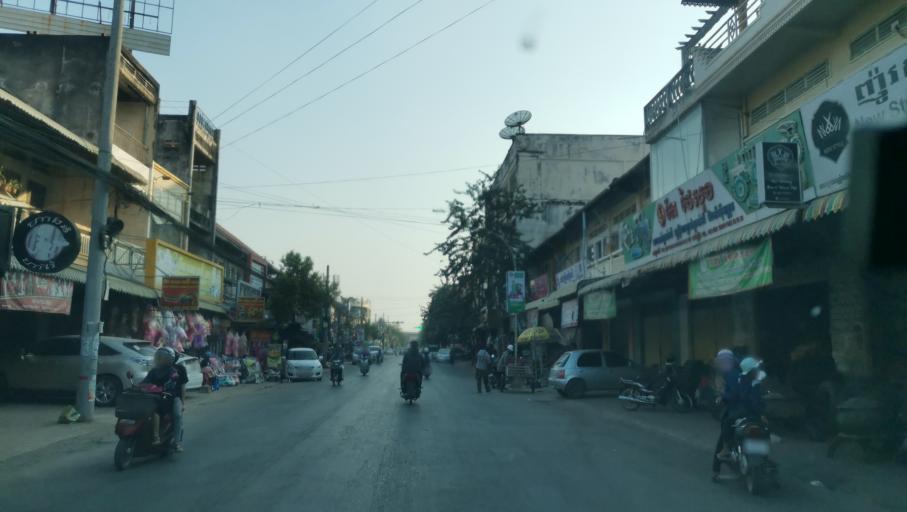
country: KH
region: Battambang
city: Battambang
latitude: 13.0989
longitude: 103.1970
